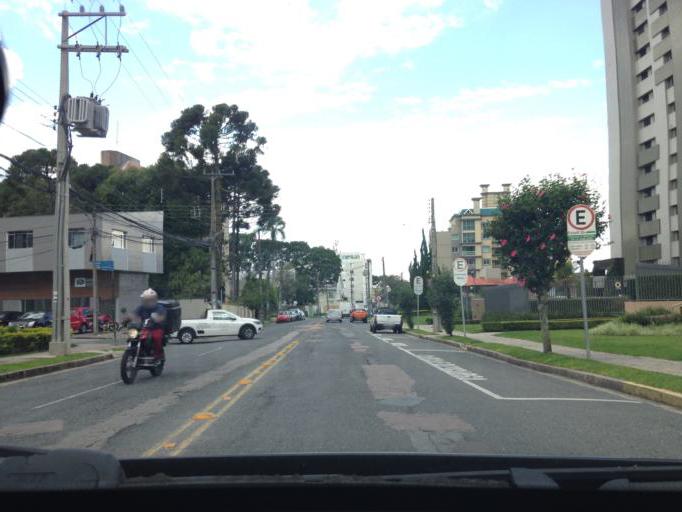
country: BR
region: Parana
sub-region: Curitiba
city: Curitiba
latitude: -25.4063
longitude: -49.2433
